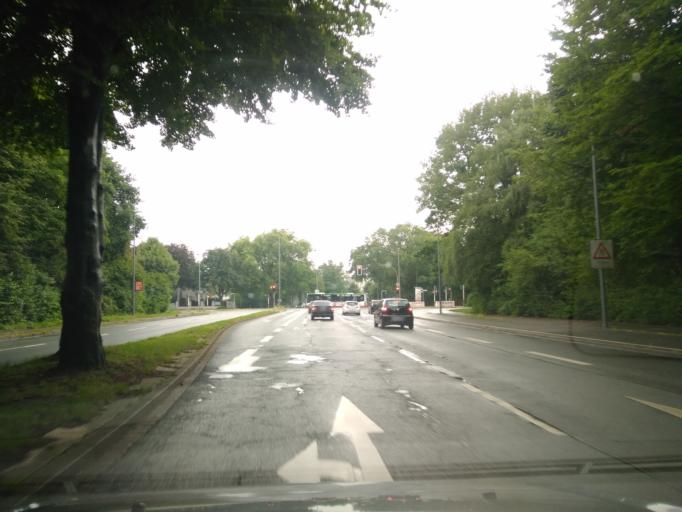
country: DE
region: North Rhine-Westphalia
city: Herten
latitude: 51.5810
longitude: 7.0670
